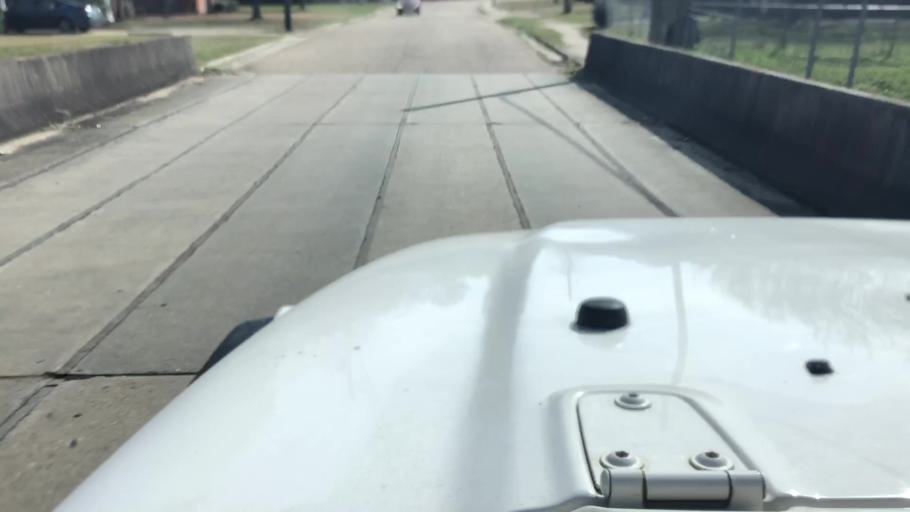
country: US
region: Alabama
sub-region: Elmore County
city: Blue Ridge
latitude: 32.4054
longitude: -86.1870
